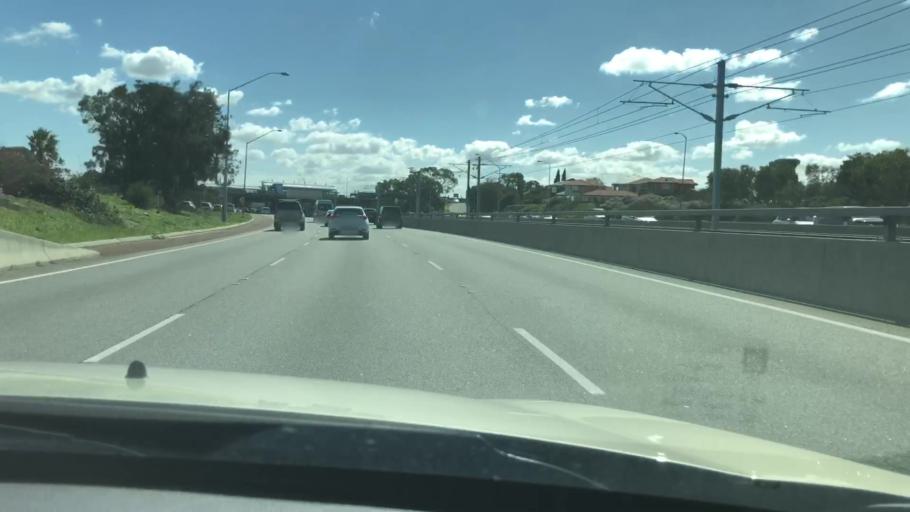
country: AU
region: Western Australia
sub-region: South Perth
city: Manning
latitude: -32.0131
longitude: 115.8573
